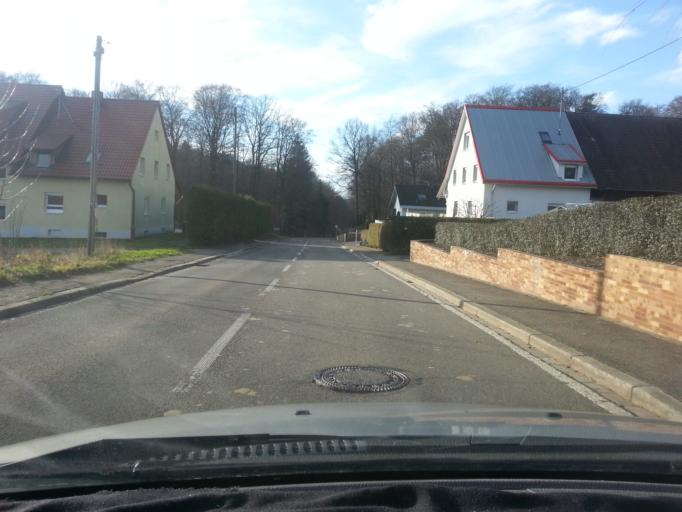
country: DE
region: Baden-Wuerttemberg
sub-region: Karlsruhe Region
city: Ostringen
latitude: 49.2020
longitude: 8.7551
